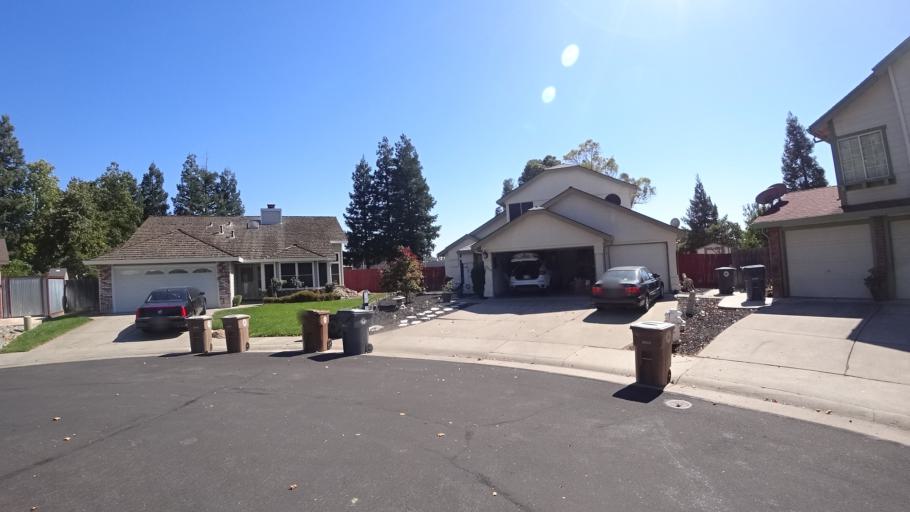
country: US
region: California
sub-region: Sacramento County
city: Laguna
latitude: 38.4310
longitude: -121.4291
